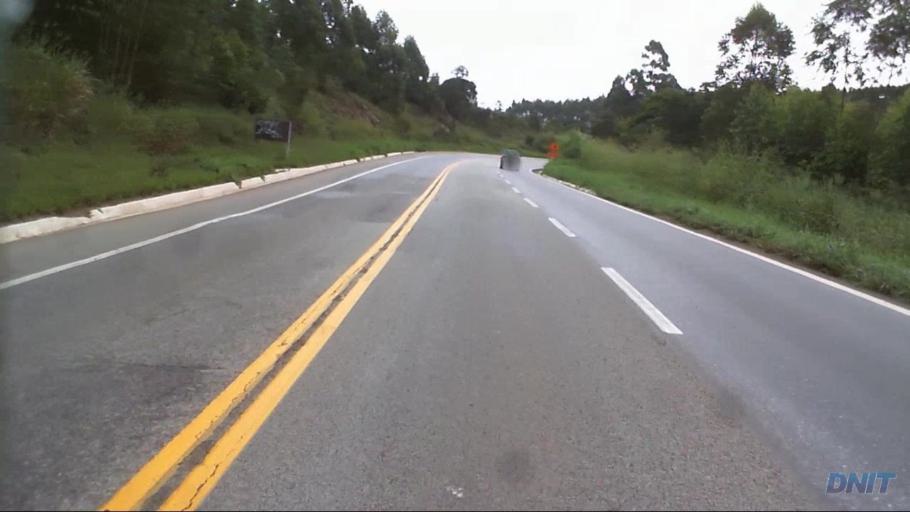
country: BR
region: Minas Gerais
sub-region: Caete
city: Caete
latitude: -19.7526
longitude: -43.5333
